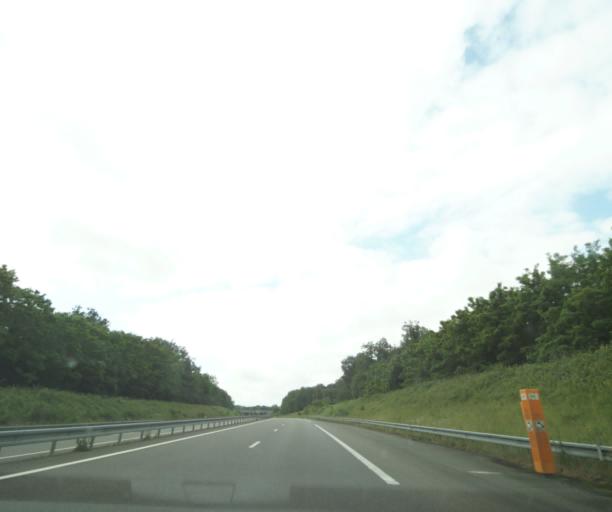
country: FR
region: Pays de la Loire
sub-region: Departement de Maine-et-Loire
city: Brion
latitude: 47.4467
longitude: -0.1770
